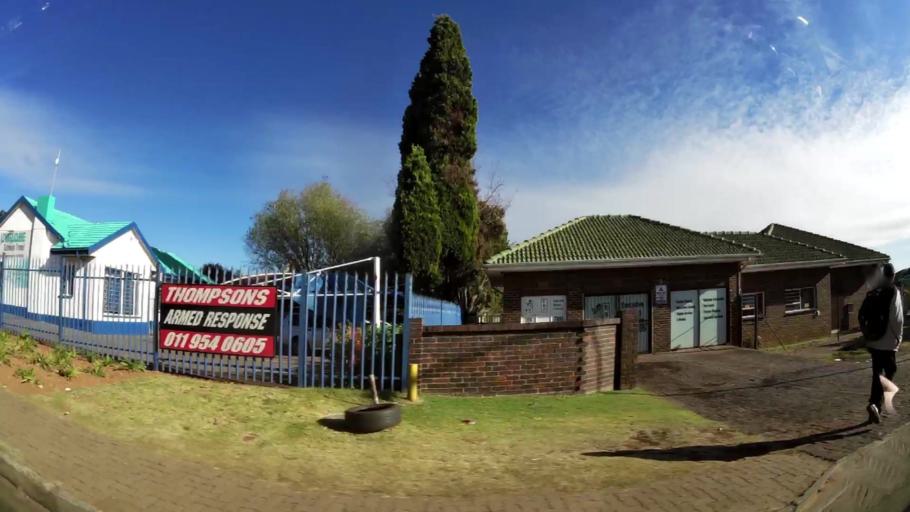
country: ZA
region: Gauteng
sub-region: City of Johannesburg Metropolitan Municipality
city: Roodepoort
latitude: -26.1242
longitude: 27.8469
